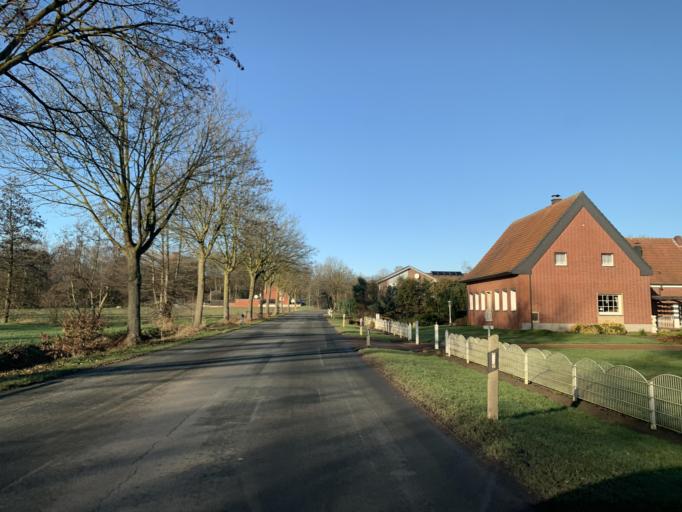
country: DE
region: North Rhine-Westphalia
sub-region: Regierungsbezirk Munster
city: Dulmen
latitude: 51.8509
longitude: 7.2918
